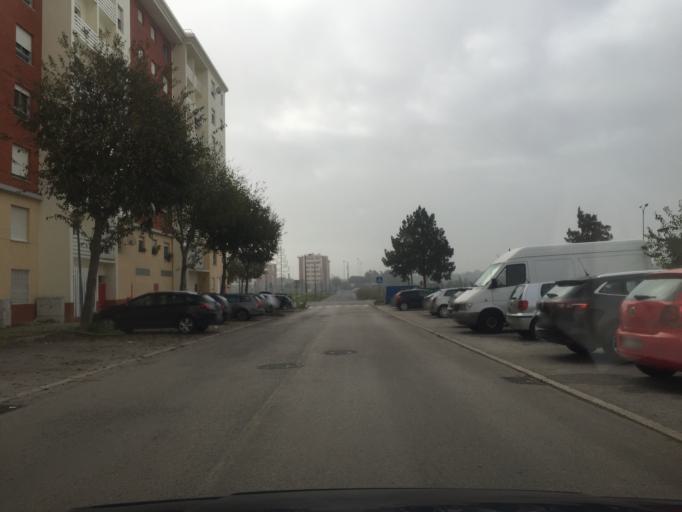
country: PT
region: Lisbon
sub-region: Odivelas
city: Olival do Basto
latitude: 38.7778
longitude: -9.1458
